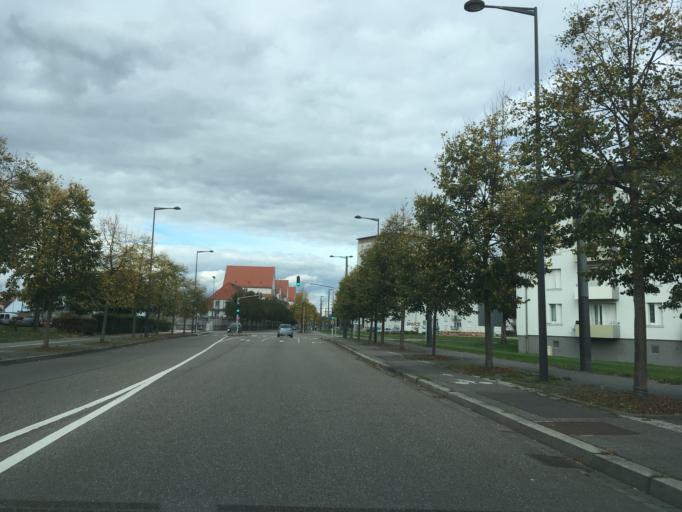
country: FR
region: Alsace
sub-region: Departement du Bas-Rhin
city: Strasbourg
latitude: 48.5465
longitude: 7.7656
